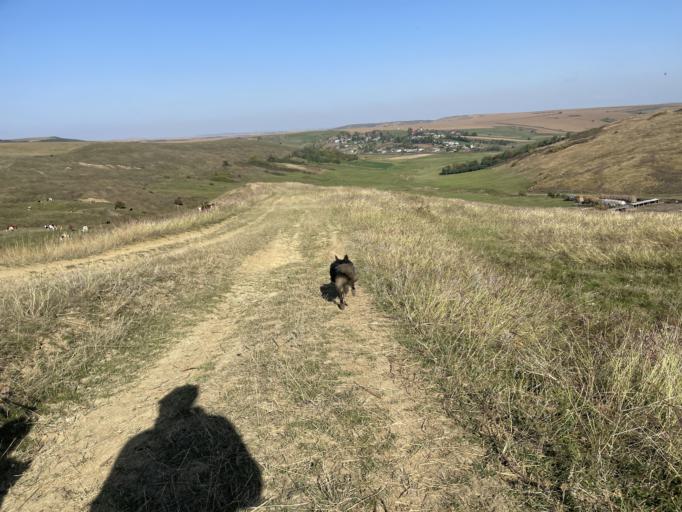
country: RO
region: Iasi
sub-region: Comuna Dumesti
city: Pausesti
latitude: 47.1520
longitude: 27.3103
